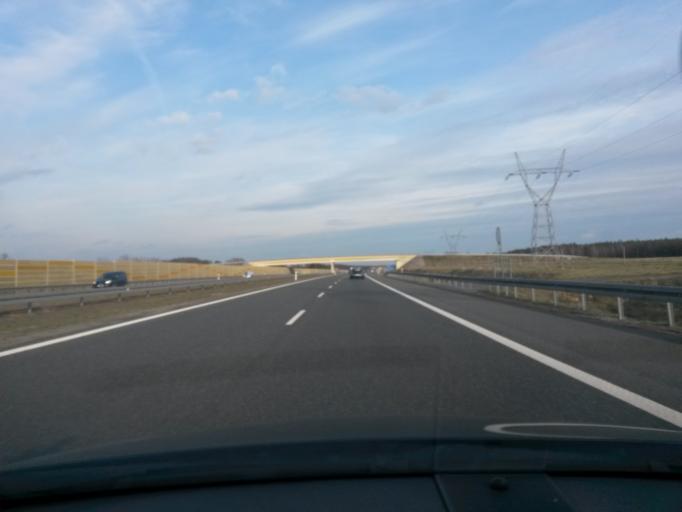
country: PL
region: Lodz Voivodeship
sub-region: Powiat zgierski
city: Ozorkow
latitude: 51.9274
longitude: 19.3177
